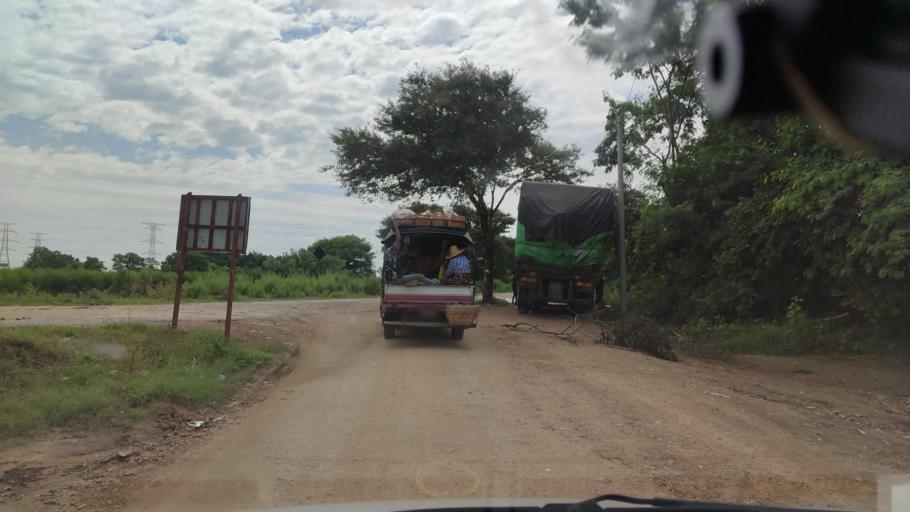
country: MM
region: Mandalay
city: Meiktila
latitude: 20.9455
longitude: 95.7735
